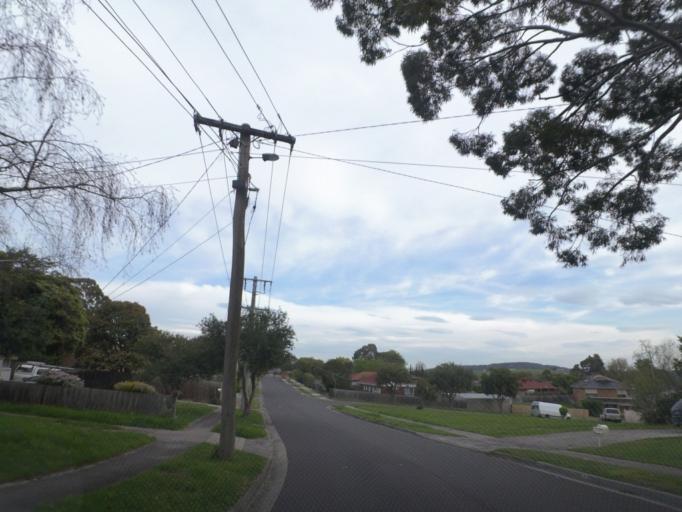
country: AU
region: Victoria
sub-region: Knox
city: Ferntree Gully
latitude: -37.8970
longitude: 145.2881
